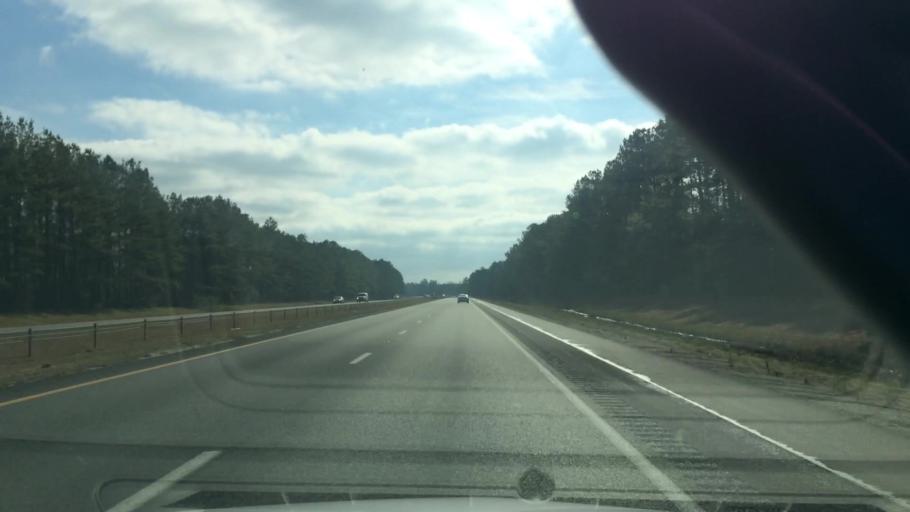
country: US
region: North Carolina
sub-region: Pender County
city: Rocky Point
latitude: 34.4725
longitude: -77.8796
